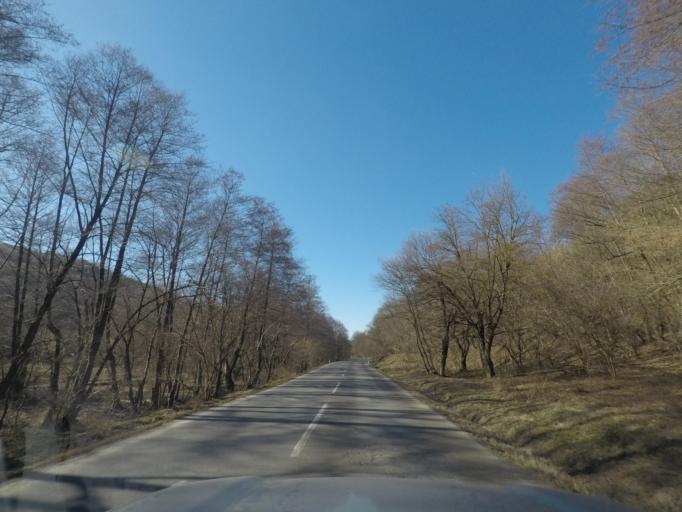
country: SK
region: Presovsky
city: Snina
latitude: 48.9912
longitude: 22.2405
